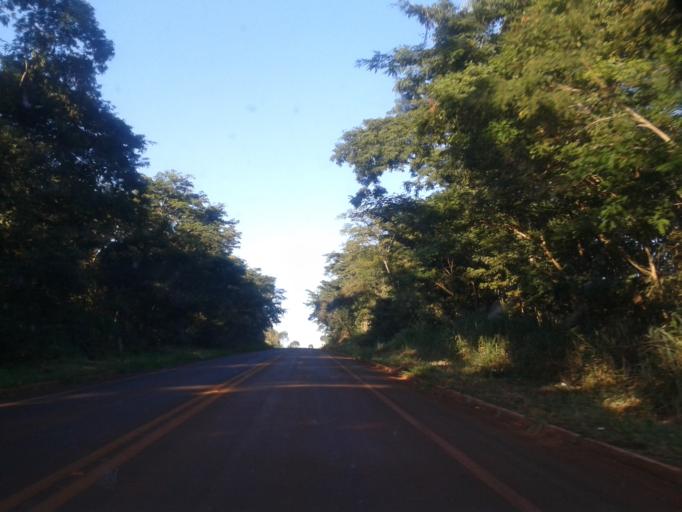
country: BR
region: Minas Gerais
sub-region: Capinopolis
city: Capinopolis
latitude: -18.6880
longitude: -49.6083
